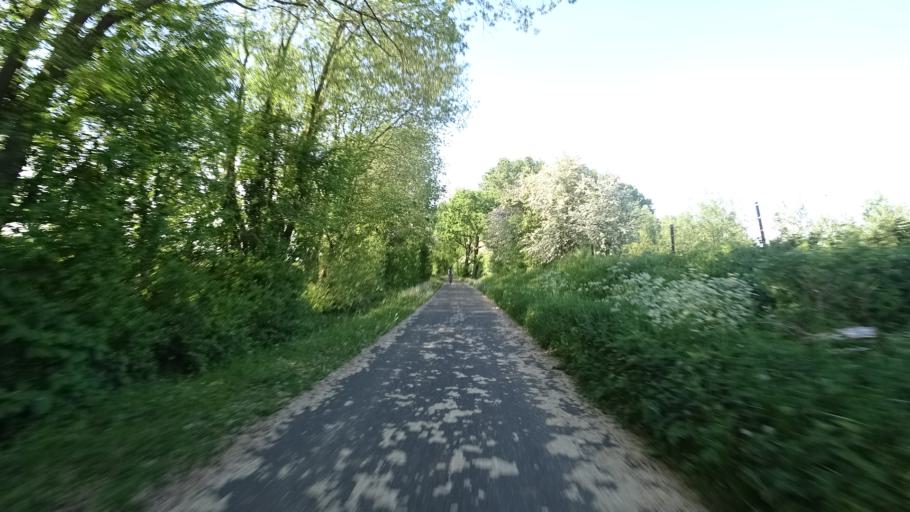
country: BE
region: Wallonia
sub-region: Province de Namur
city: Eghezee
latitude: 50.5287
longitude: 4.9000
